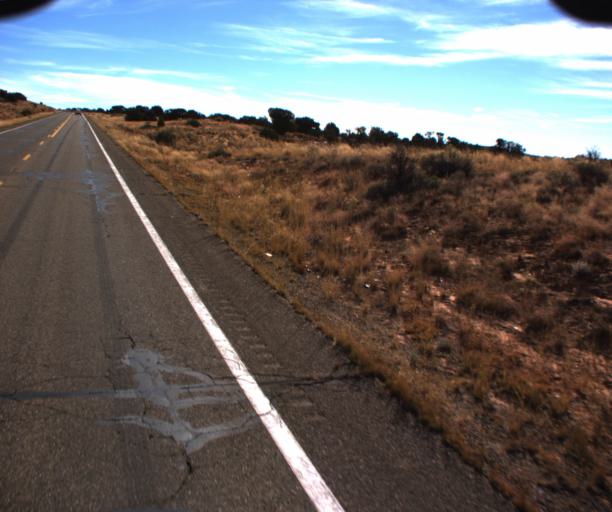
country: US
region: Arizona
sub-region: Coconino County
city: Kaibito
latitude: 36.5781
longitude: -111.1313
